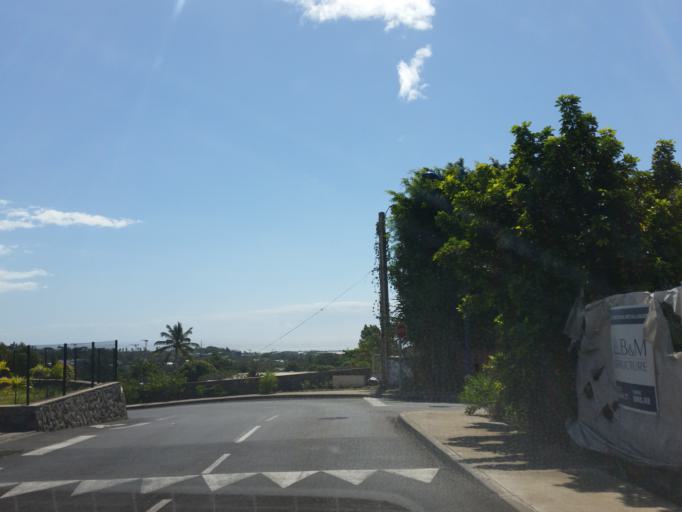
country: RE
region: Reunion
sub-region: Reunion
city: Sainte-Marie
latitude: -20.9176
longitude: 55.5143
